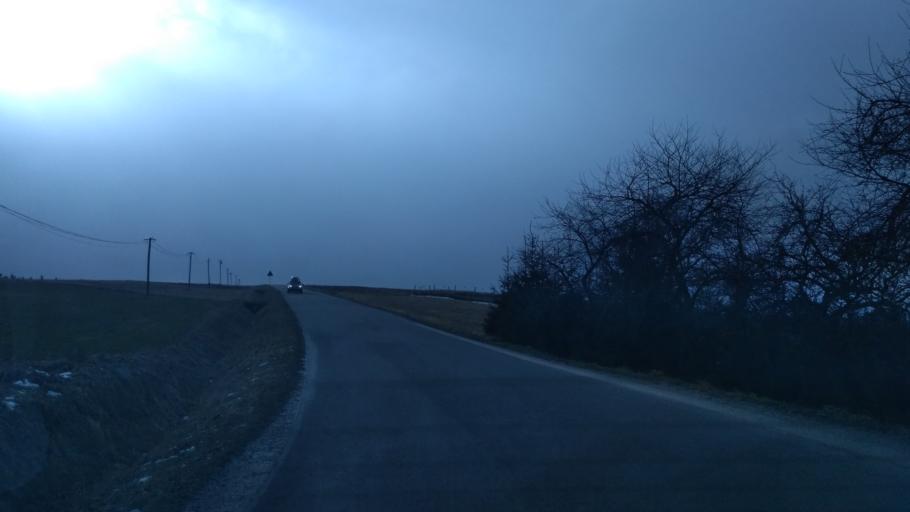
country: PL
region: Subcarpathian Voivodeship
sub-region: Powiat rzeszowski
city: Blazowa
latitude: 49.8497
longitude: 22.0869
